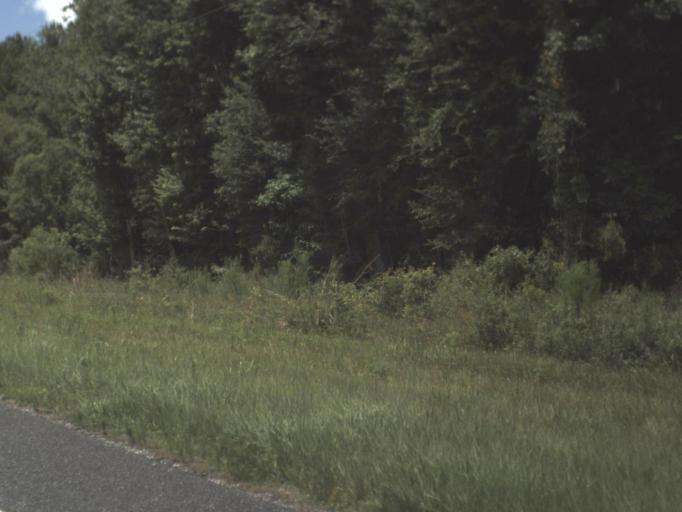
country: US
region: Florida
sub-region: Taylor County
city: Perry
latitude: 30.2781
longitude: -83.7252
